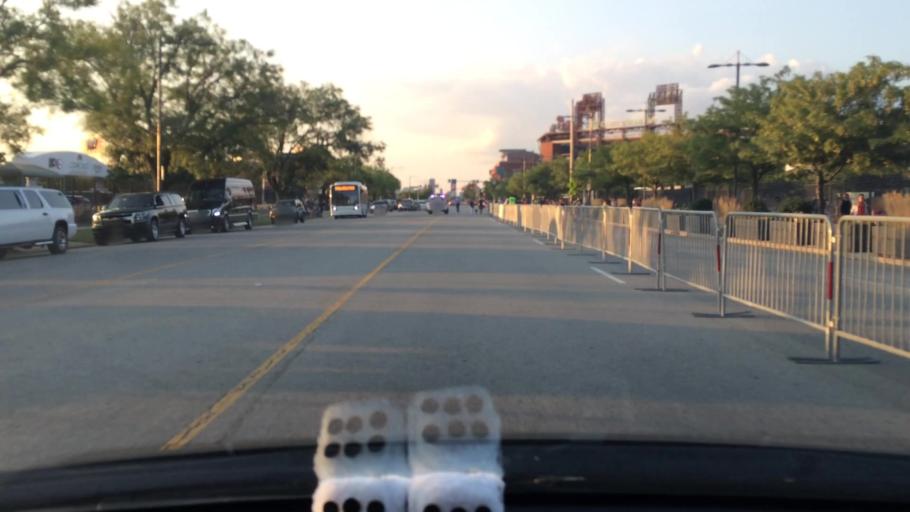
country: US
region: New Jersey
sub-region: Gloucester County
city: National Park
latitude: 39.9023
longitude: -75.1691
